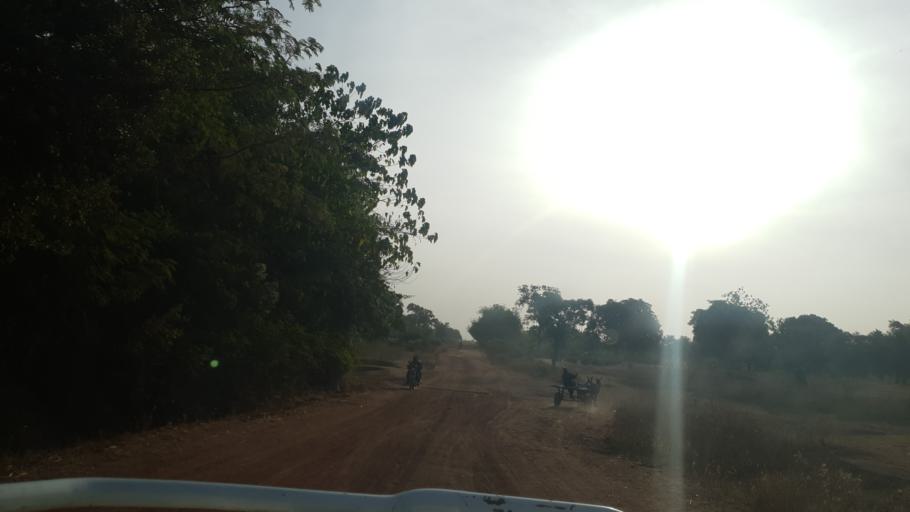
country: ML
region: Koulikoro
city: Dioila
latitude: 12.7707
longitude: -6.9324
